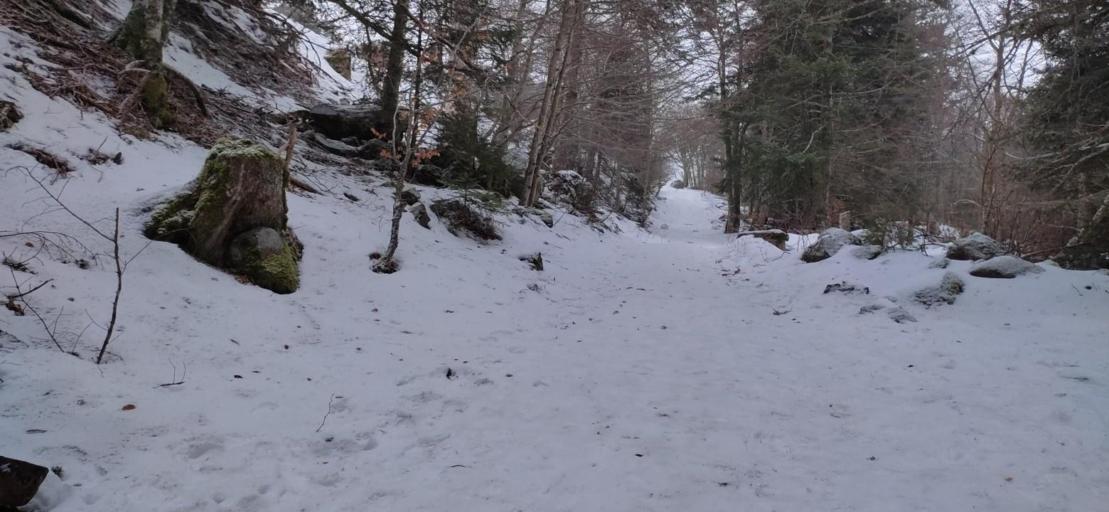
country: FR
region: Auvergne
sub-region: Departement du Puy-de-Dome
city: Mont-Dore
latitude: 45.5492
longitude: 2.8151
